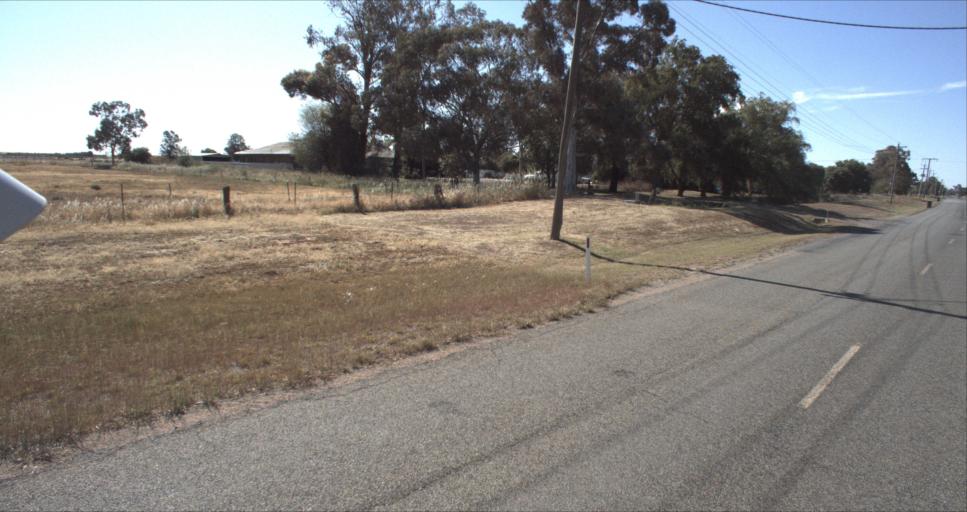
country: AU
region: New South Wales
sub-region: Leeton
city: Leeton
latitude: -34.5653
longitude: 146.3828
